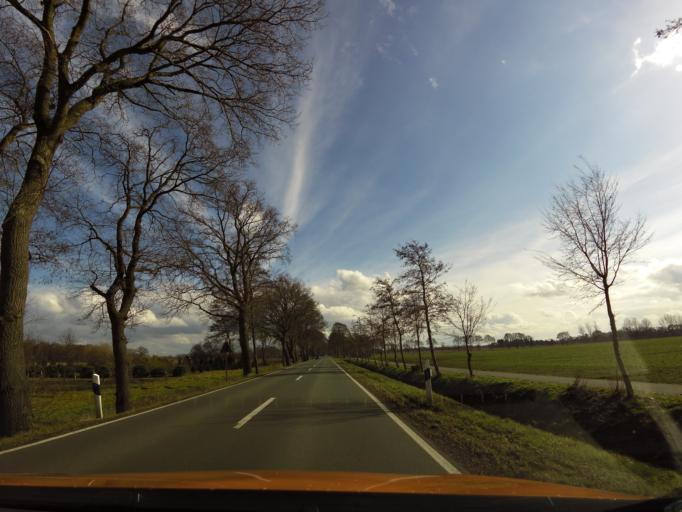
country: DE
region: Lower Saxony
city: Hatten
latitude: 53.0763
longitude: 8.2974
